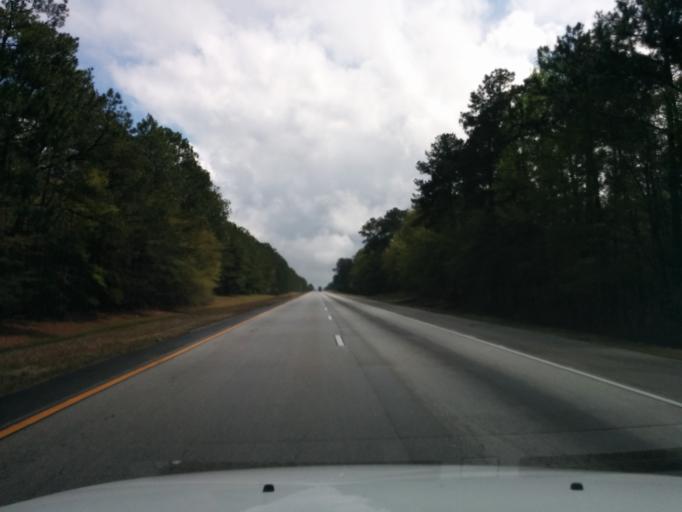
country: US
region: Georgia
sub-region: Candler County
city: Metter
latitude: 32.3427
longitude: -81.9625
